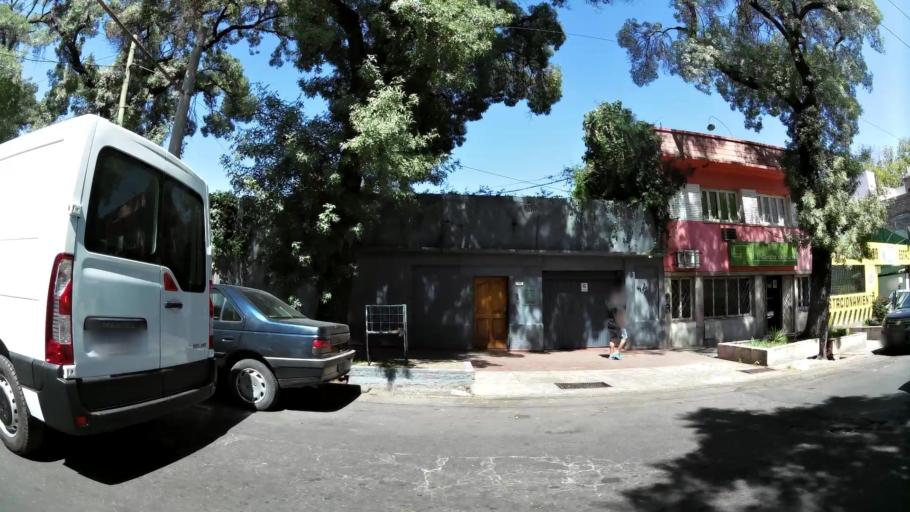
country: AR
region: Mendoza
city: Mendoza
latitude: -32.8889
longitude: -68.8308
